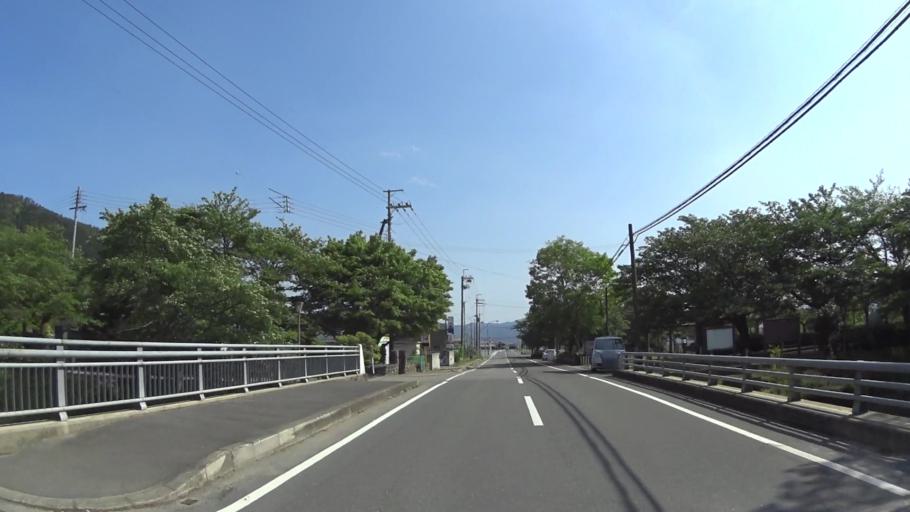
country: JP
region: Kyoto
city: Kameoka
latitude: 35.0460
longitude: 135.5837
